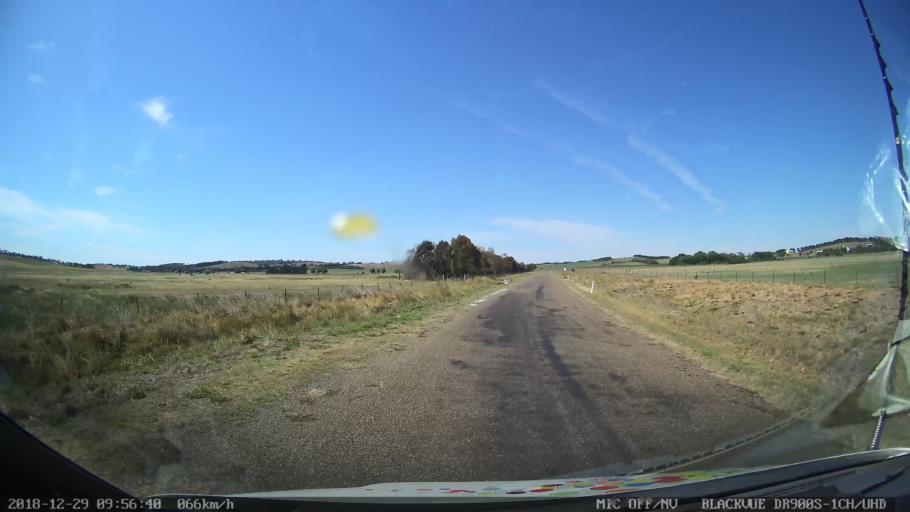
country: AU
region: New South Wales
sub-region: Goulburn Mulwaree
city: Goulburn
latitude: -34.7794
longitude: 149.4818
